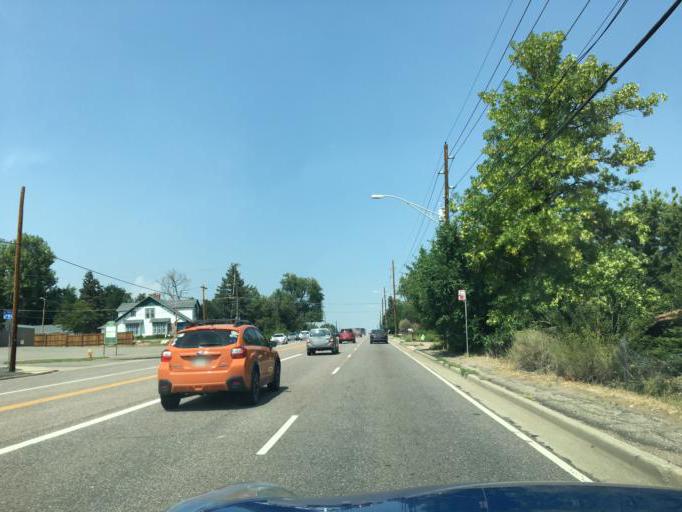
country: US
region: Colorado
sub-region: Jefferson County
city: Wheat Ridge
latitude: 39.7437
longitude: -105.1095
